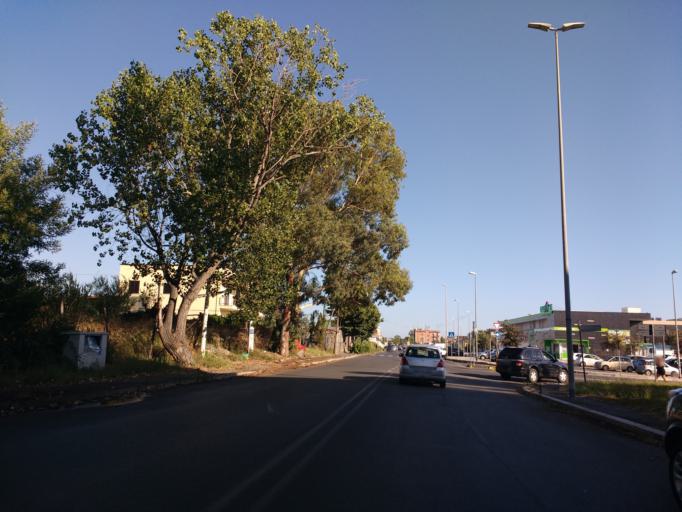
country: IT
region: Latium
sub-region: Citta metropolitana di Roma Capitale
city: Acilia-Castel Fusano-Ostia Antica
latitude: 41.7739
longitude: 12.3536
